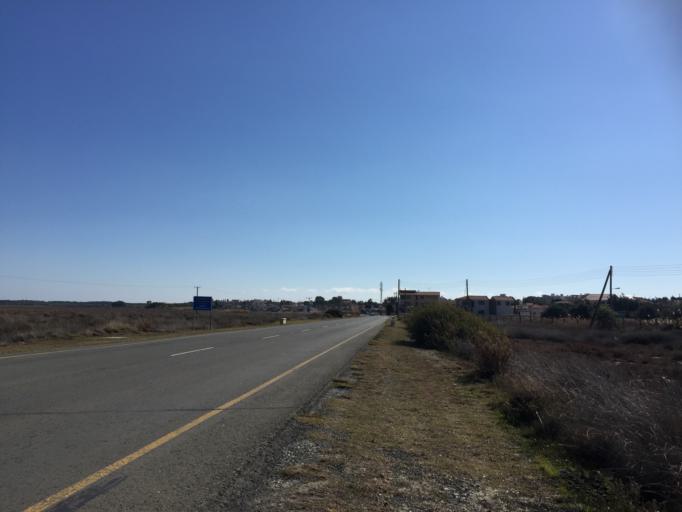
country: CY
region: Larnaka
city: Kolossi
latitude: 34.6076
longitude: 32.9488
